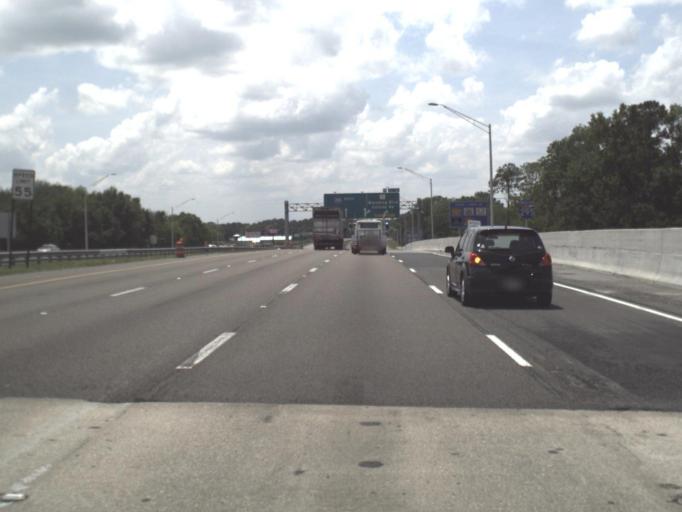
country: US
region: Florida
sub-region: Clay County
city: Orange Park
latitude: 30.1916
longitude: -81.7115
